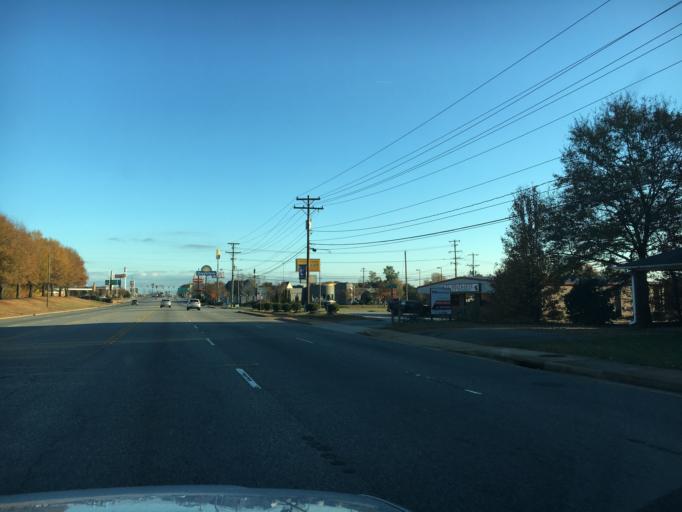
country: US
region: South Carolina
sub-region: Spartanburg County
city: Lyman
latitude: 34.9188
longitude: -82.1132
